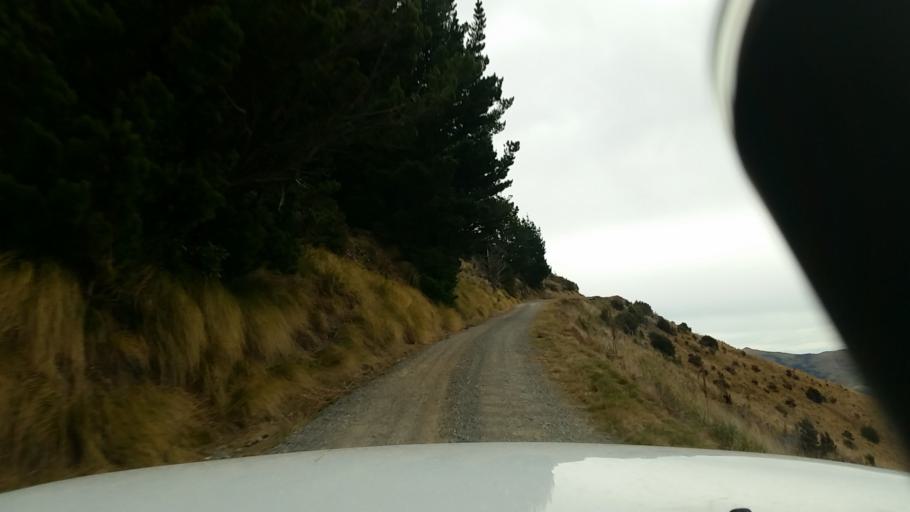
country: NZ
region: Canterbury
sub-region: Christchurch City
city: Christchurch
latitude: -43.8108
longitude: 172.8329
